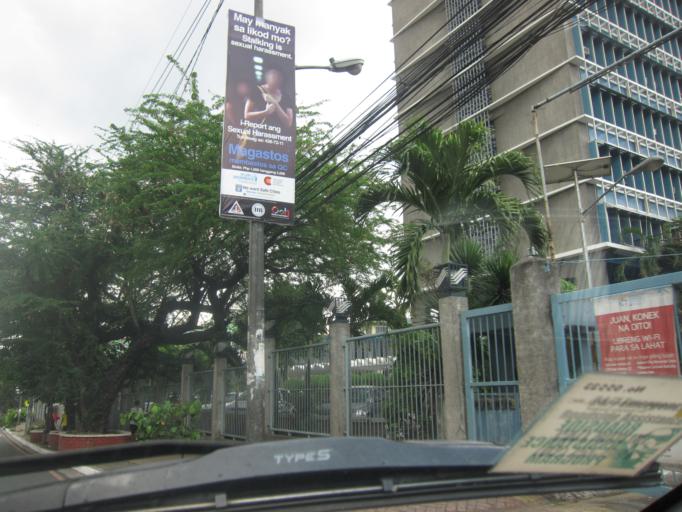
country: PH
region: Metro Manila
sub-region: Quezon City
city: Quezon City
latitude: 14.6397
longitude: 121.0467
